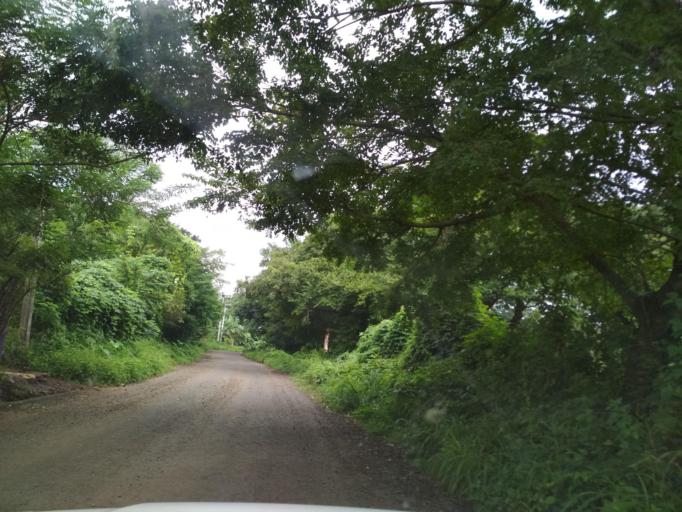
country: MX
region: Veracruz
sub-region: San Andres Tuxtla
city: Matacapan
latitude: 18.4448
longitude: -95.1799
